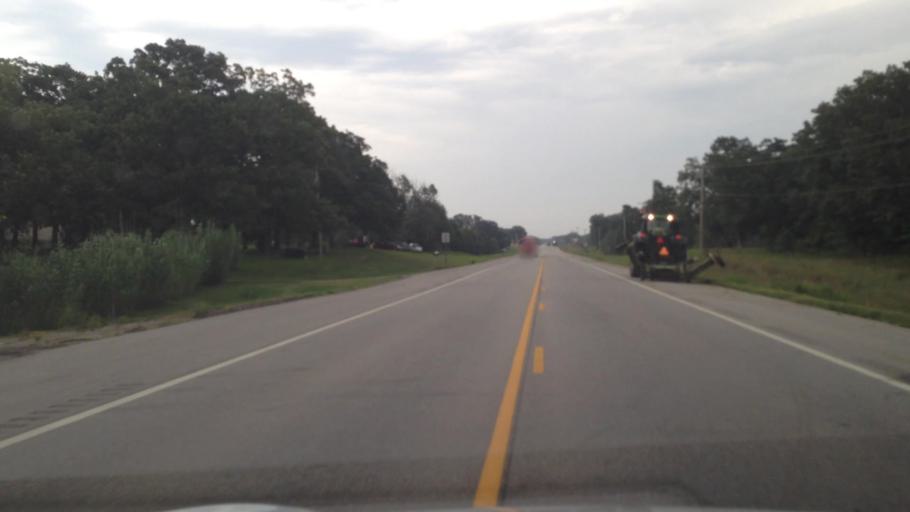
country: US
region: Kansas
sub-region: Cherokee County
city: Galena
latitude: 37.0236
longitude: -94.6605
